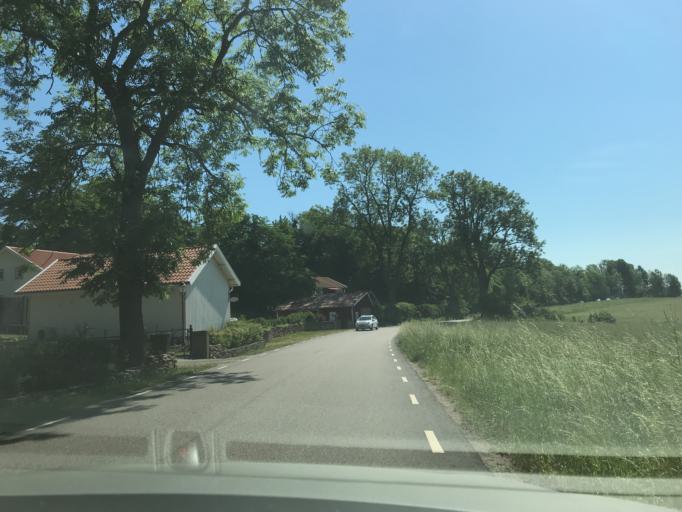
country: SE
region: Vaestra Goetaland
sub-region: Gotene Kommun
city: Kallby
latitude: 58.5551
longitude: 13.3465
